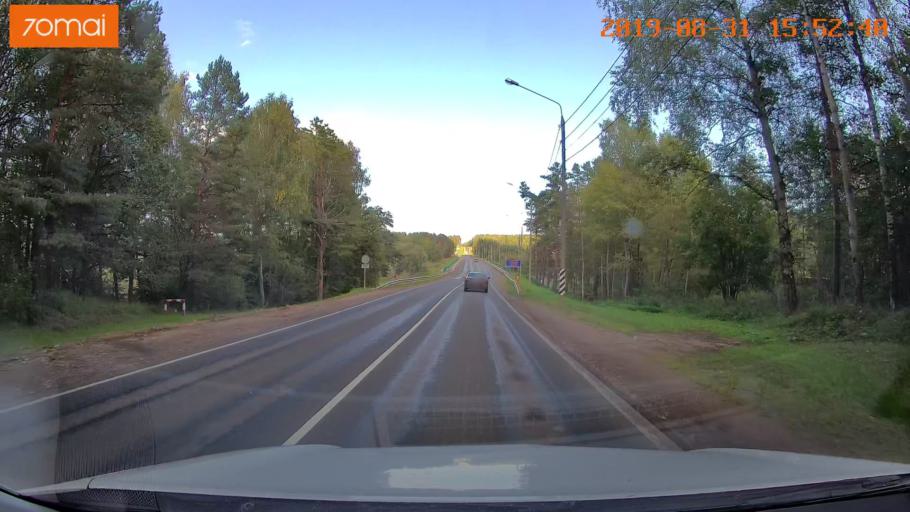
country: RU
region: Kaluga
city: Yukhnov
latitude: 54.7090
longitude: 35.1170
